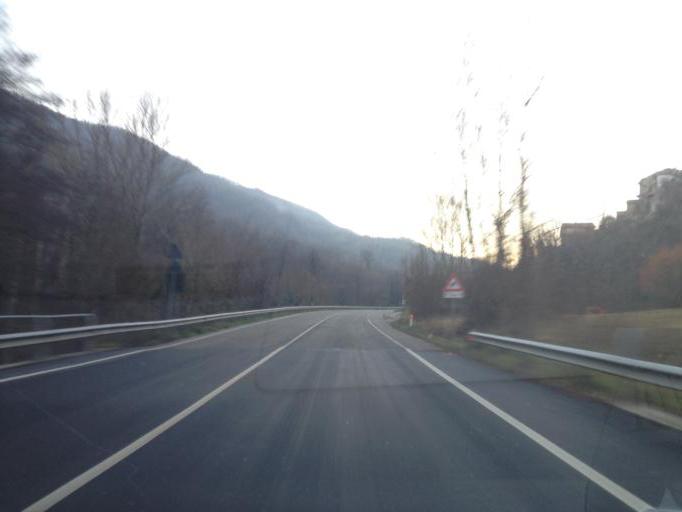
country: IT
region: The Marches
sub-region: Provincia di Ascoli Piceno
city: Arquata del Tronto
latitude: 42.7609
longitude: 13.2853
